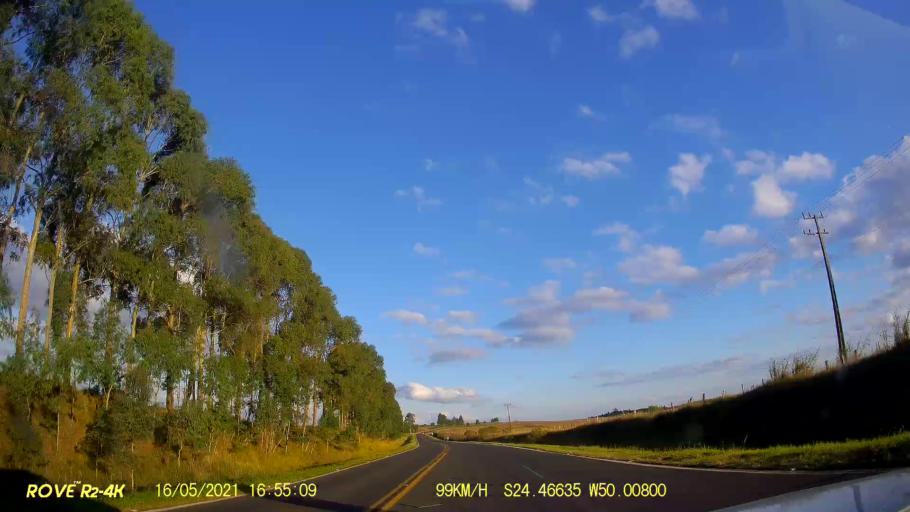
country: BR
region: Parana
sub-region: Pirai Do Sul
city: Pirai do Sul
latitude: -24.4664
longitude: -50.0080
